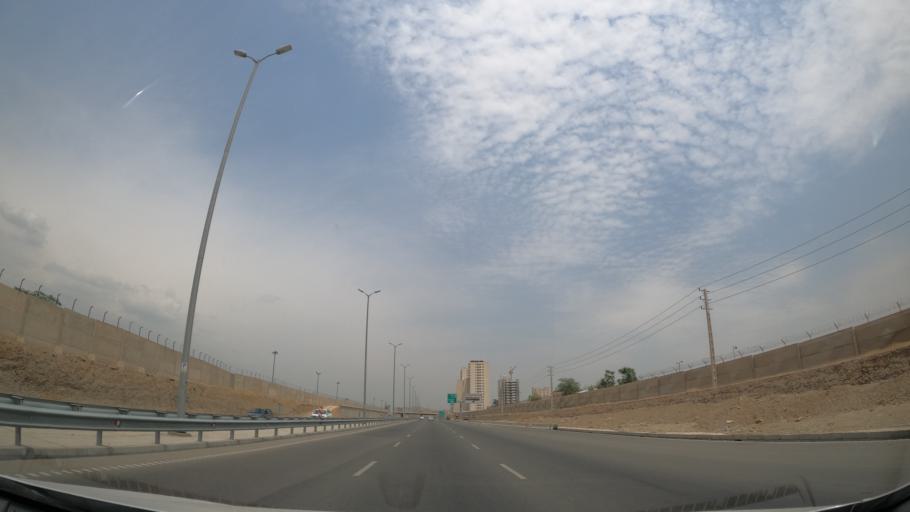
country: IR
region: Tehran
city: Shahr-e Qods
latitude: 35.7406
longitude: 51.2367
